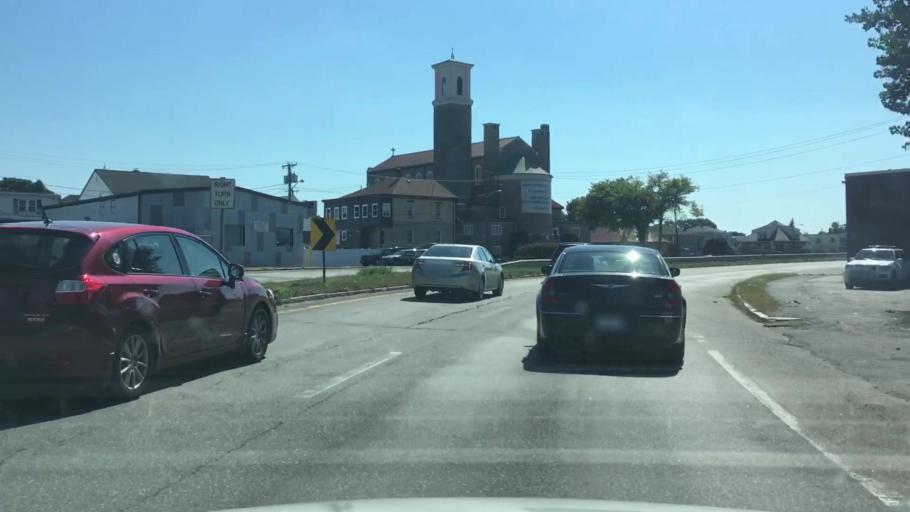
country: US
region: Massachusetts
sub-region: Suffolk County
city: Revere
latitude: 42.4198
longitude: -71.0023
